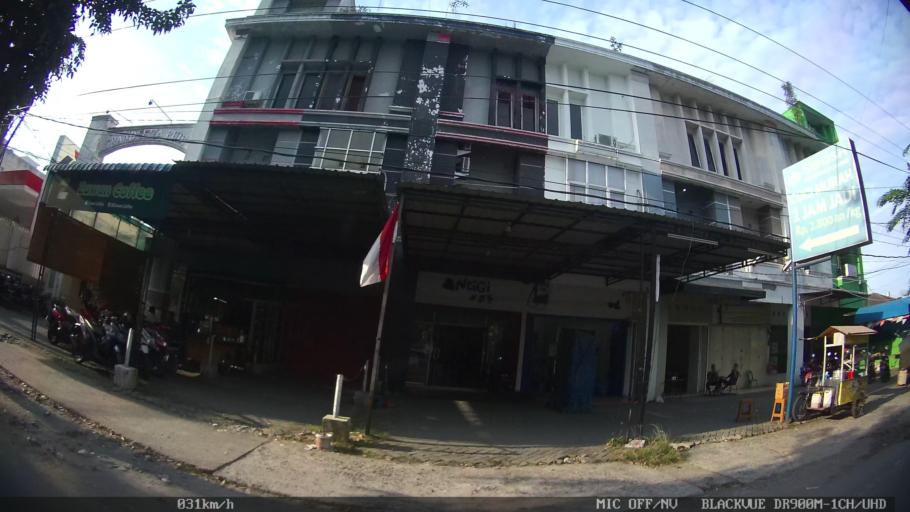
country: ID
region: North Sumatra
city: Medan
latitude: 3.5775
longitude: 98.6435
